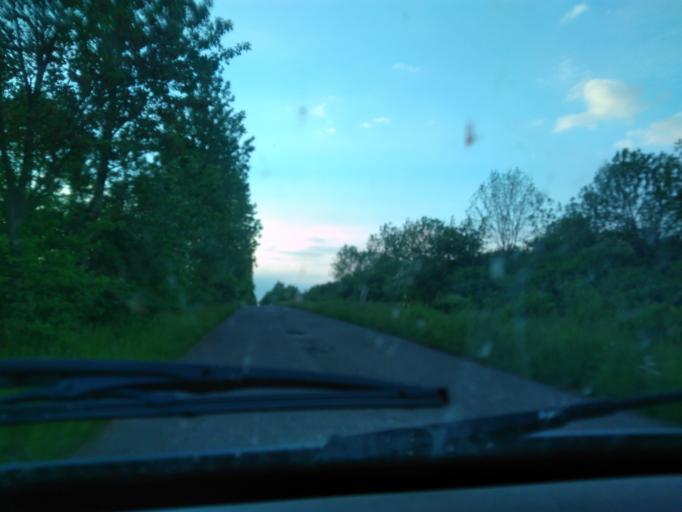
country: DE
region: Saxony-Anhalt
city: Naumburg
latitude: 51.1167
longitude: 11.8162
